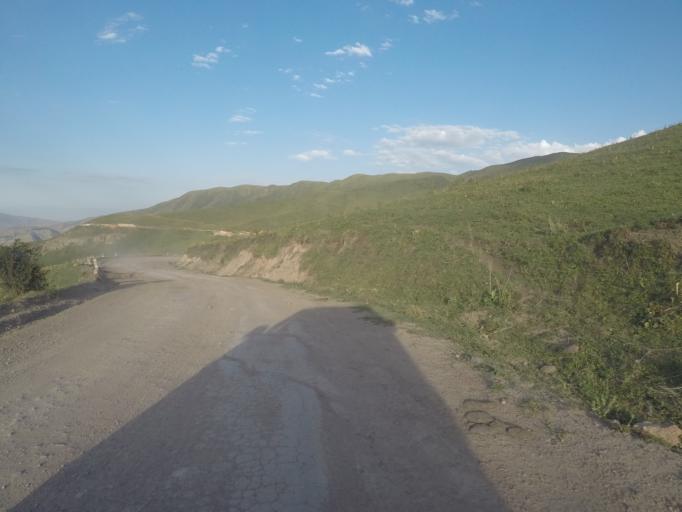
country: KG
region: Chuy
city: Bishkek
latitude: 42.6419
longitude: 74.6318
